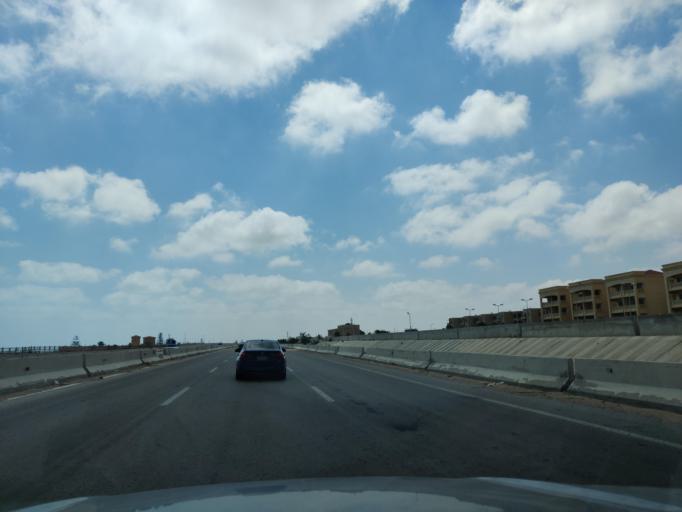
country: EG
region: Muhafazat Matruh
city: Al `Alamayn
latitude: 30.8209
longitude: 29.0129
